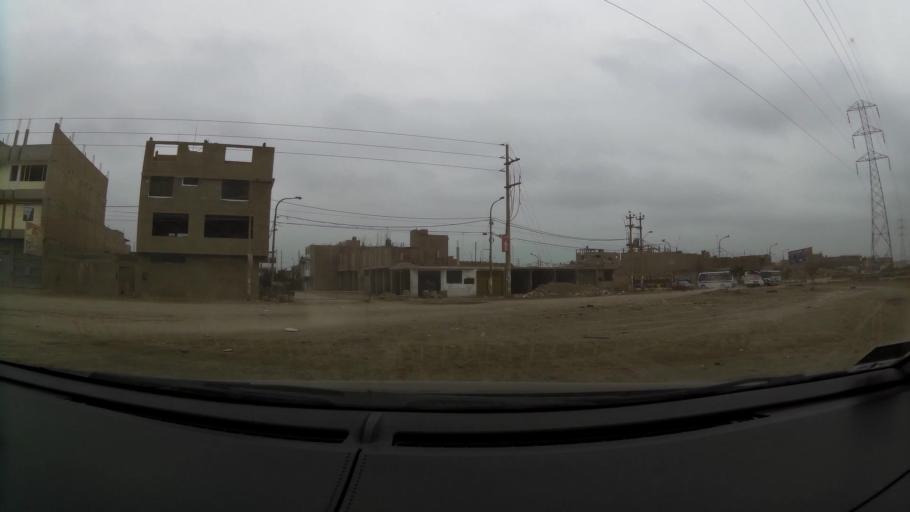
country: PE
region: Lima
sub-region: Lima
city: Independencia
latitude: -11.9676
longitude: -77.0934
